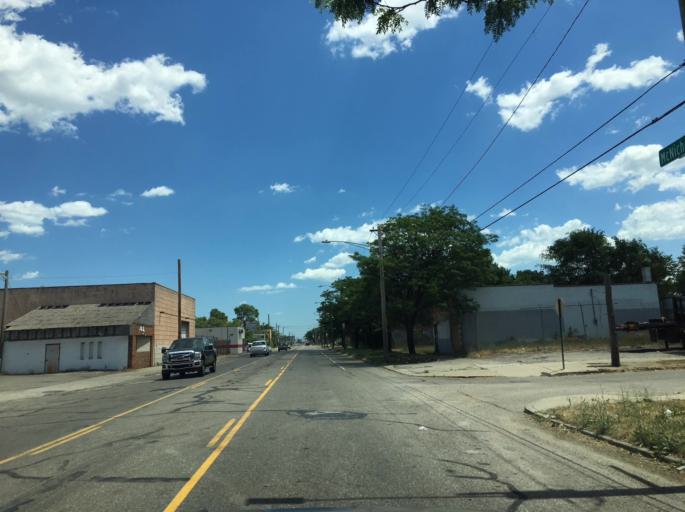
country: US
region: Michigan
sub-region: Wayne County
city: Hamtramck
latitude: 42.4189
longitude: -83.0500
